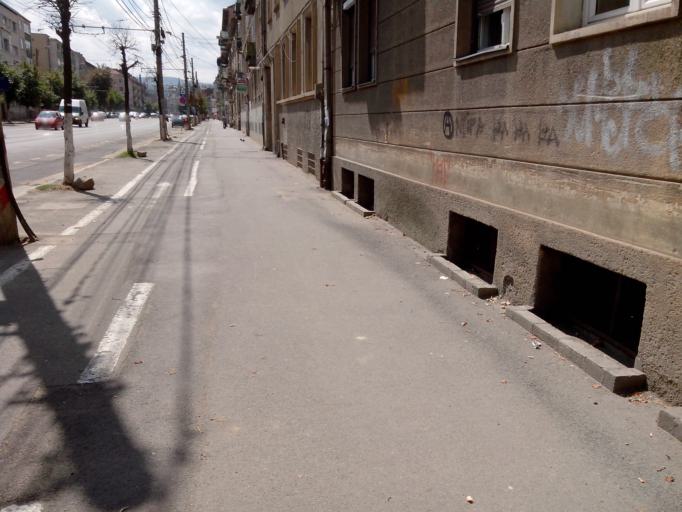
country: RO
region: Cluj
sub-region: Municipiul Cluj-Napoca
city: Cluj-Napoca
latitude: 46.7797
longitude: 23.5874
